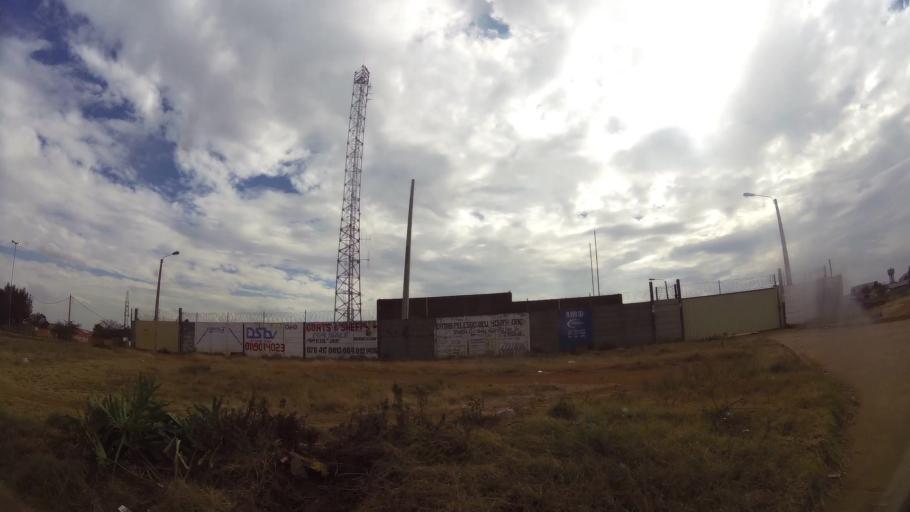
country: ZA
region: Gauteng
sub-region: Ekurhuleni Metropolitan Municipality
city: Germiston
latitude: -26.3991
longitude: 28.1488
